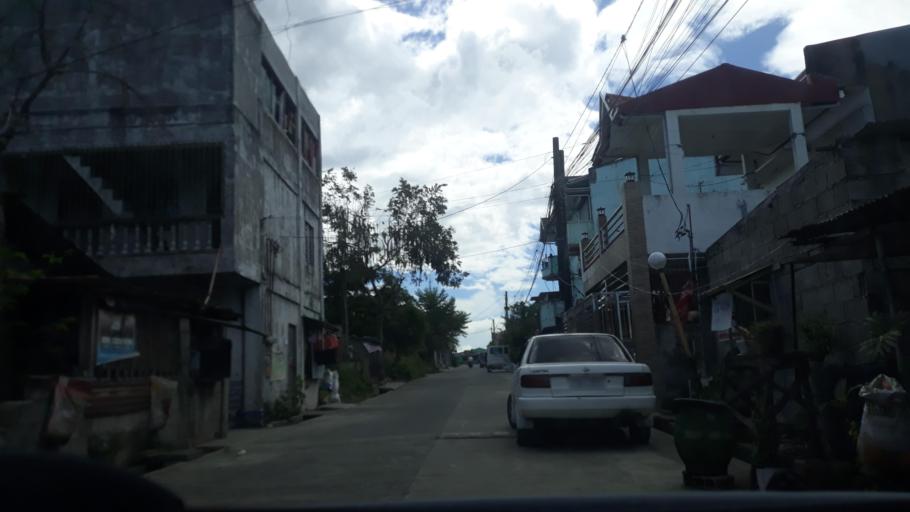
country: PH
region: Calabarzon
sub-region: Province of Cavite
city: Bulihan
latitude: 14.3045
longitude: 120.9723
